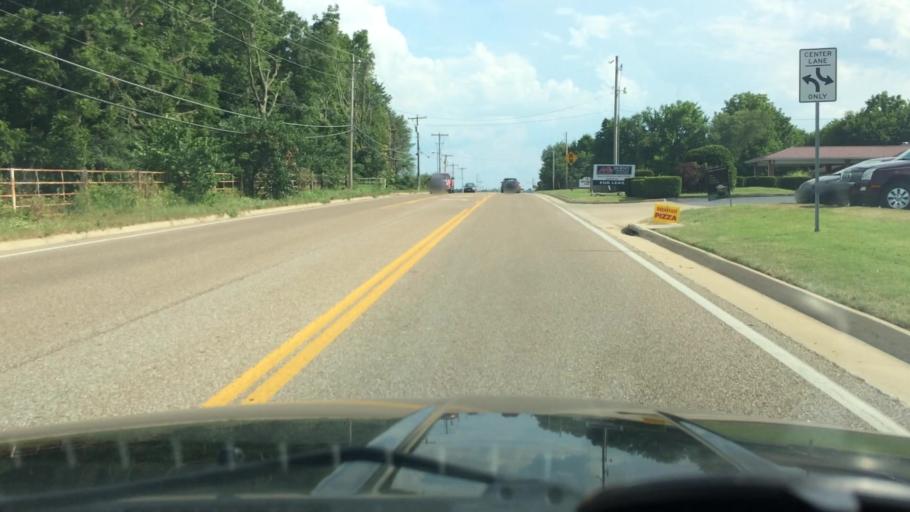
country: US
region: Missouri
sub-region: Greene County
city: Springfield
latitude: 37.2656
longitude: -93.2647
